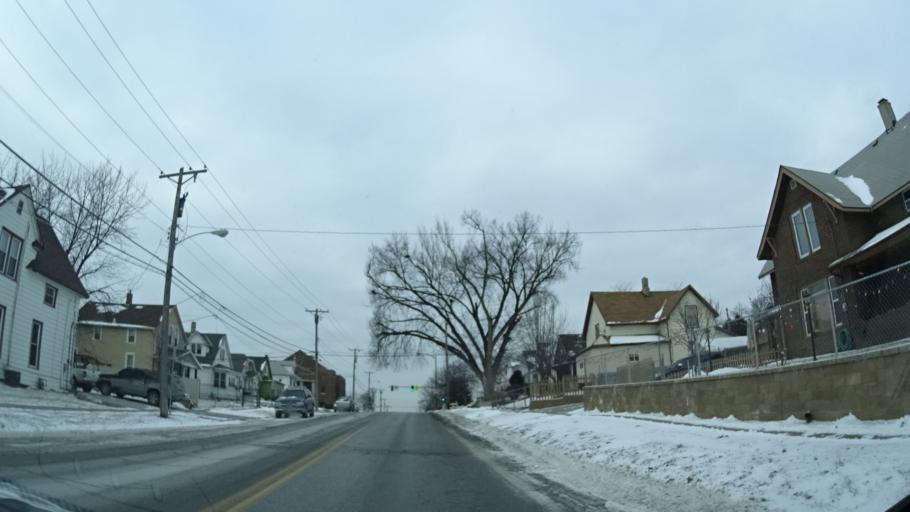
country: US
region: Nebraska
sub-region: Douglas County
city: Omaha
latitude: 41.2197
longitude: -95.9487
